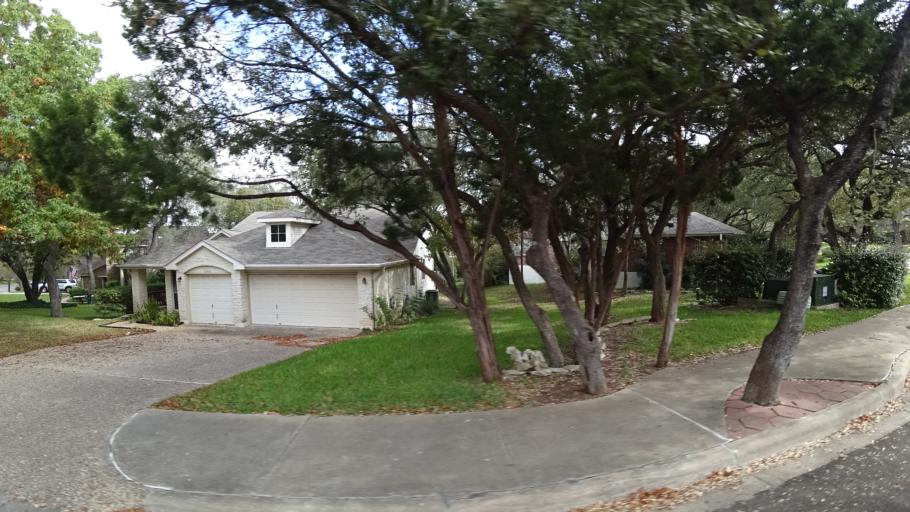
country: US
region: Texas
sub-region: Williamson County
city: Anderson Mill
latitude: 30.4204
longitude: -97.8603
